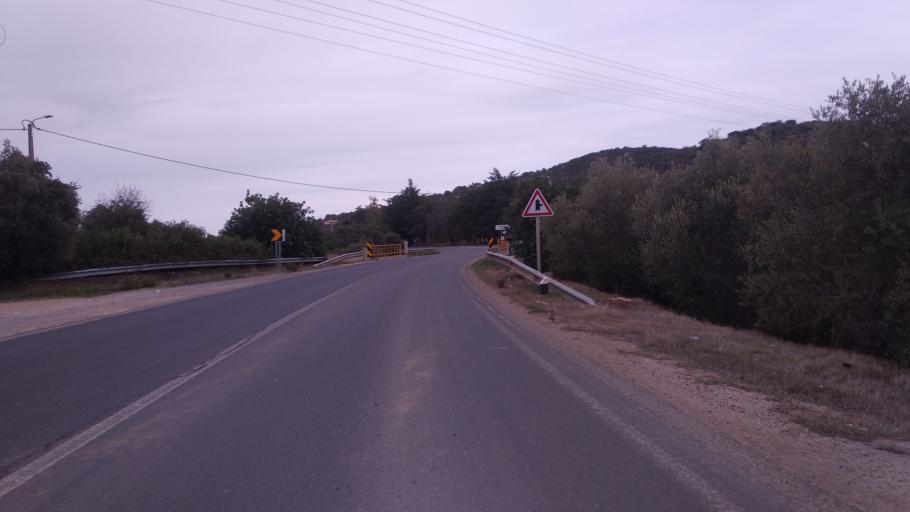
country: PT
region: Faro
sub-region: Faro
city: Santa Barbara de Nexe
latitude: 37.1492
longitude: -7.9527
